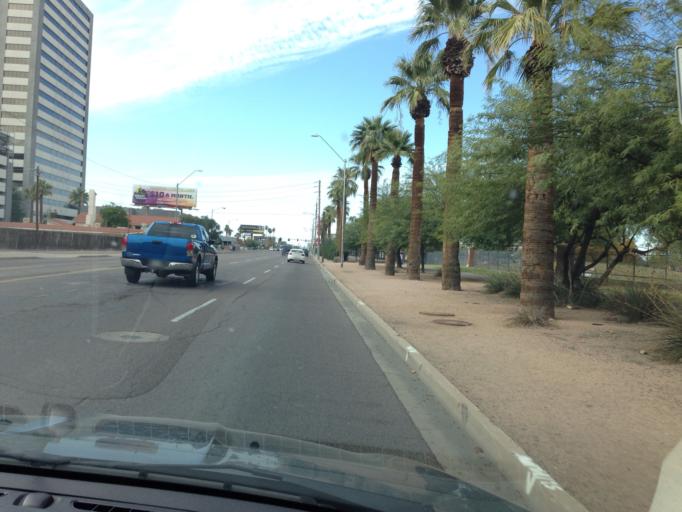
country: US
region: Arizona
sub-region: Maricopa County
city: Phoenix
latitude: 33.4949
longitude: -112.0704
